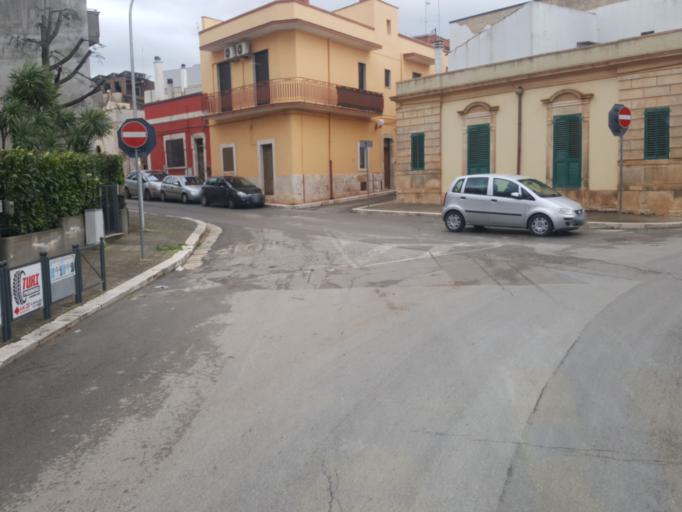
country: IT
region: Apulia
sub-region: Provincia di Bari
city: Turi
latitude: 40.9164
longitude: 17.0249
